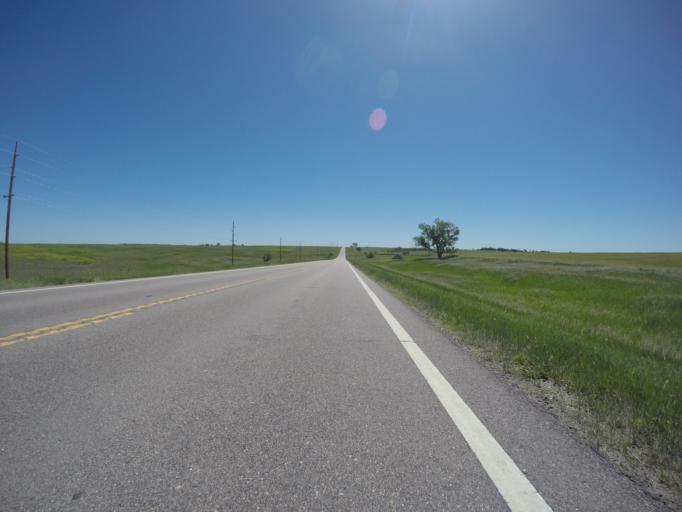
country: US
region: Kansas
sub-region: Norton County
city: Norton
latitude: 39.8284
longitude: -99.6699
